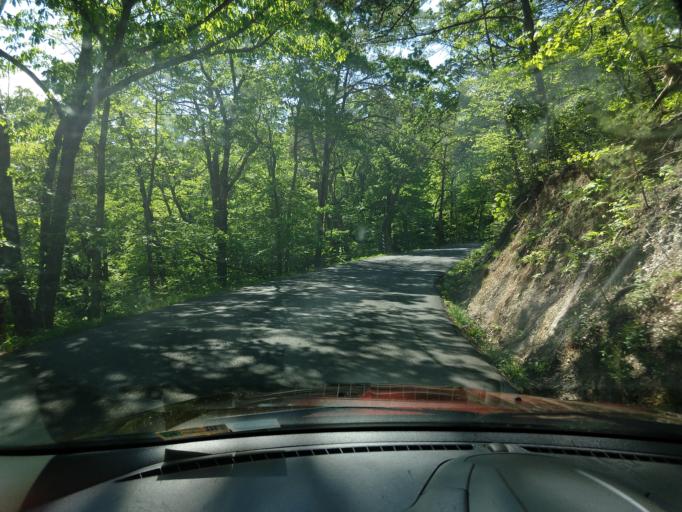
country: US
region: Virginia
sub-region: City of Covington
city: Fairlawn
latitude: 37.7128
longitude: -79.8917
